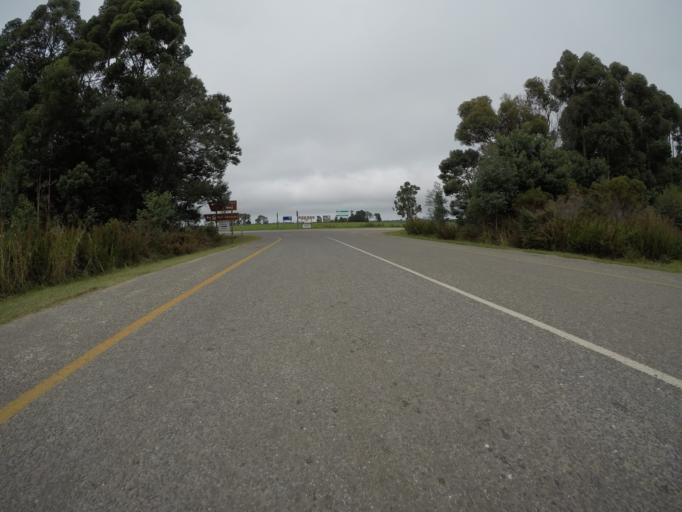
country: ZA
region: Eastern Cape
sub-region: Cacadu District Municipality
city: Kareedouw
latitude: -33.9813
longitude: 24.0424
